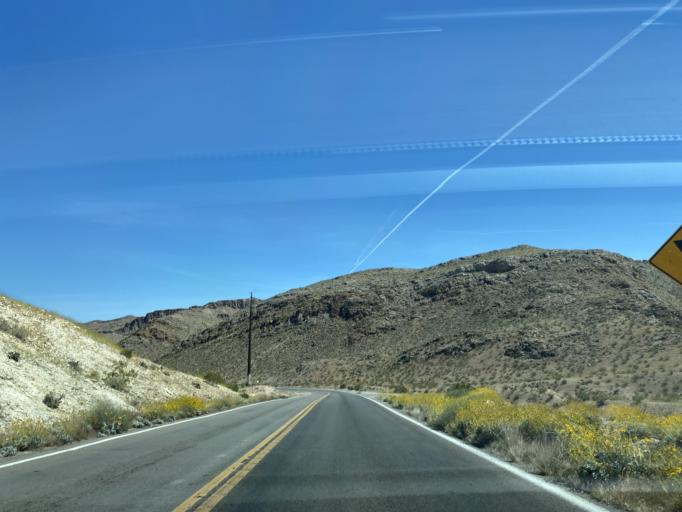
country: US
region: Nevada
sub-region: Clark County
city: Nellis Air Force Base
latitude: 36.2020
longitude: -114.9851
